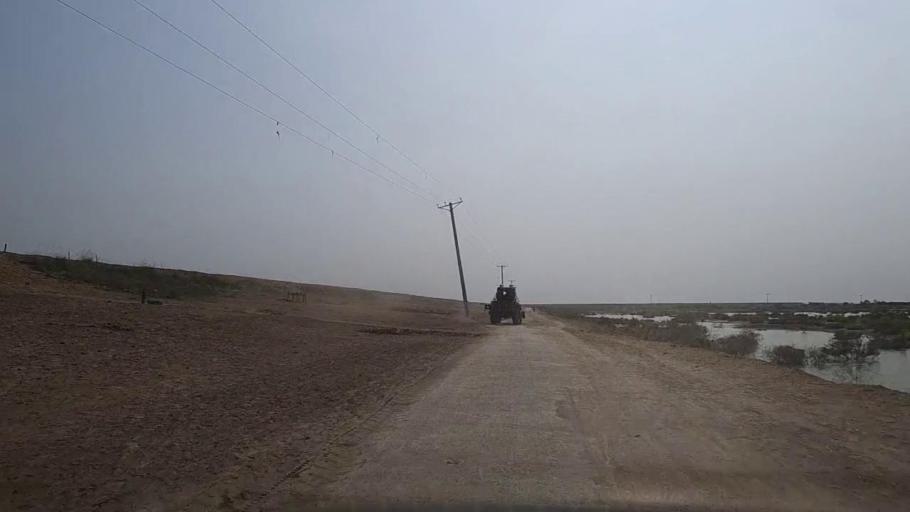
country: PK
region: Sindh
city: Thatta
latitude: 24.5781
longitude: 67.9155
